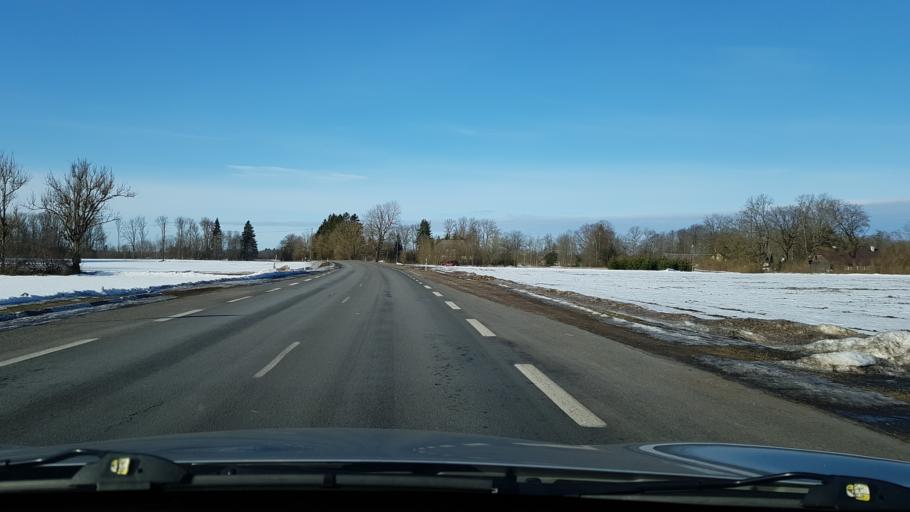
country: EE
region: Viljandimaa
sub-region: Vohma linn
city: Vohma
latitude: 58.6320
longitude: 25.6115
